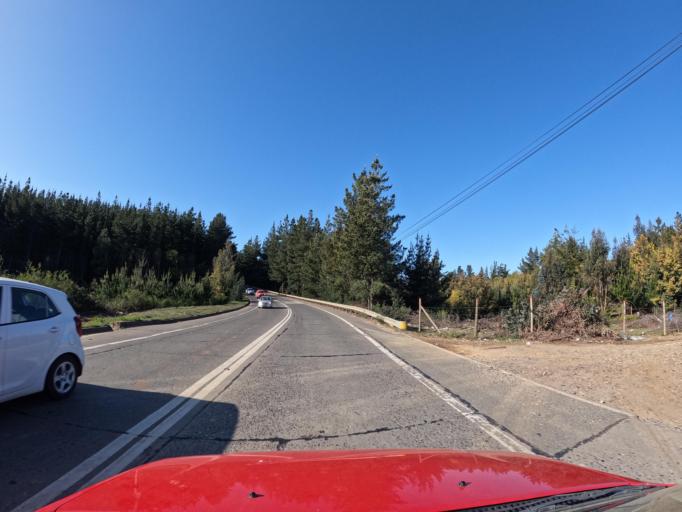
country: CL
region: Maule
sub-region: Provincia de Talca
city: Constitucion
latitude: -35.4370
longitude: -72.3348
